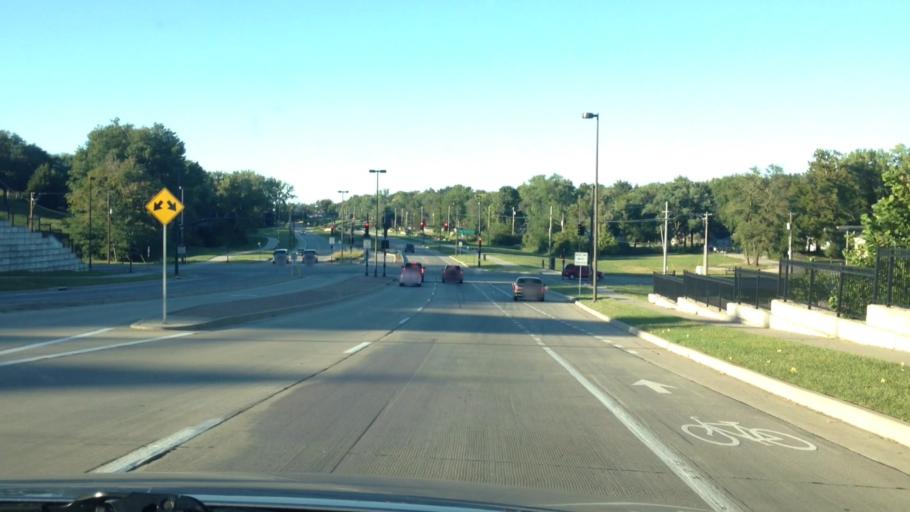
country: US
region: Missouri
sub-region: Clay County
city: North Kansas City
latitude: 39.1613
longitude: -94.5327
